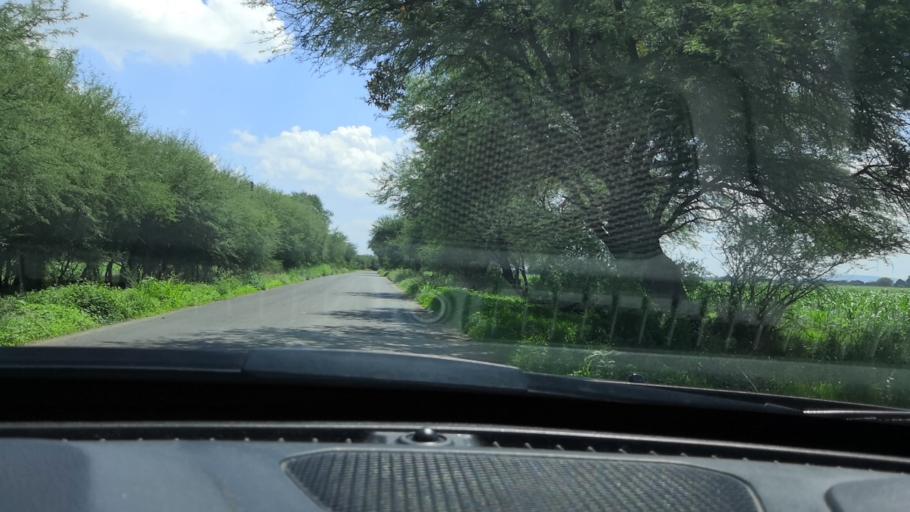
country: MX
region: Guanajuato
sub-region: Leon
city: Plan Guanajuato (La Sandia)
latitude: 20.9459
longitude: -101.6186
